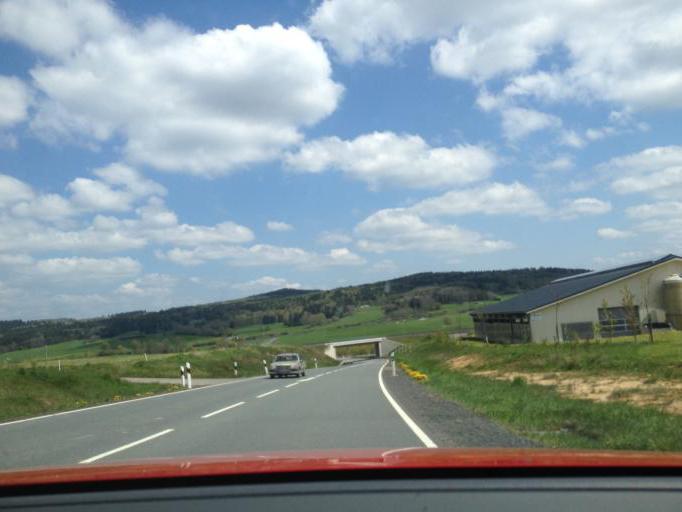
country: DE
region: Bavaria
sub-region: Upper Franconia
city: Marktredwitz
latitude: 49.9813
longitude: 12.1163
